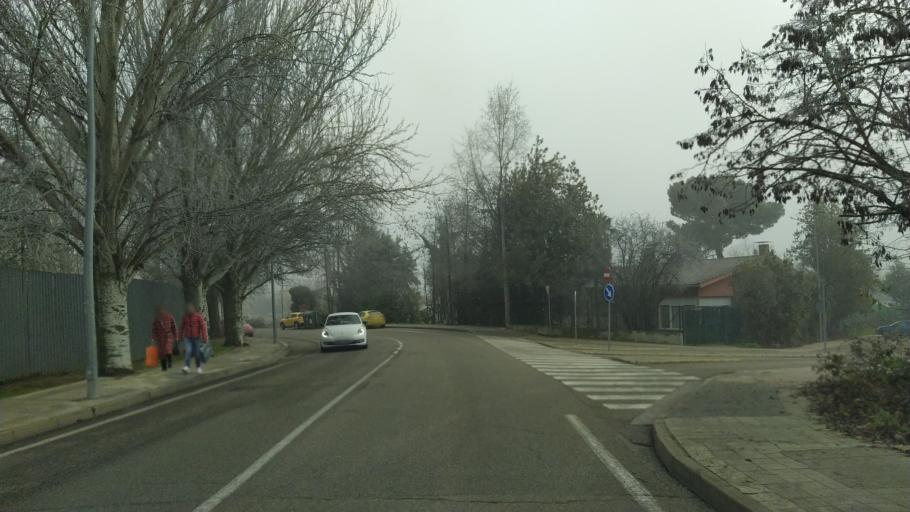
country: ES
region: Castille and Leon
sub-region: Provincia de Palencia
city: Palencia
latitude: 42.0026
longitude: -4.5359
